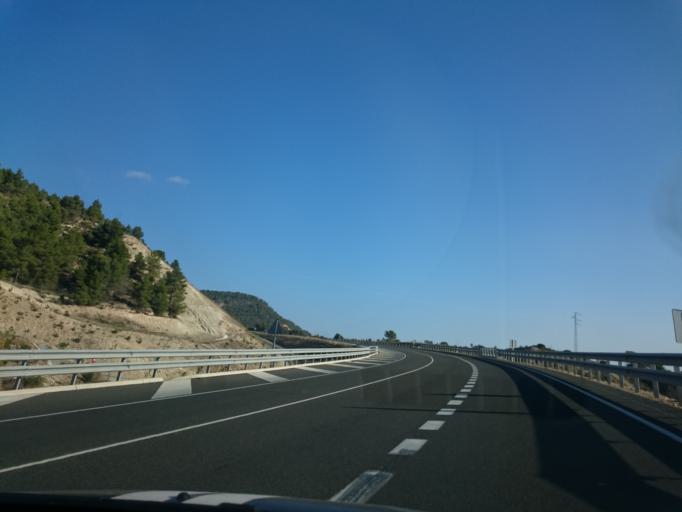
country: ES
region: Catalonia
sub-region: Provincia de Barcelona
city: Odena
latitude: 41.6009
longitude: 1.6735
